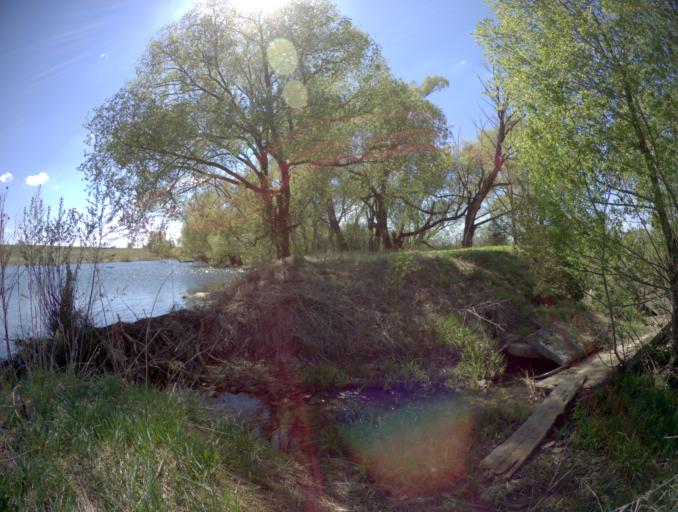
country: RU
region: Vladimir
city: Suzdal'
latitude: 56.3311
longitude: 40.3574
